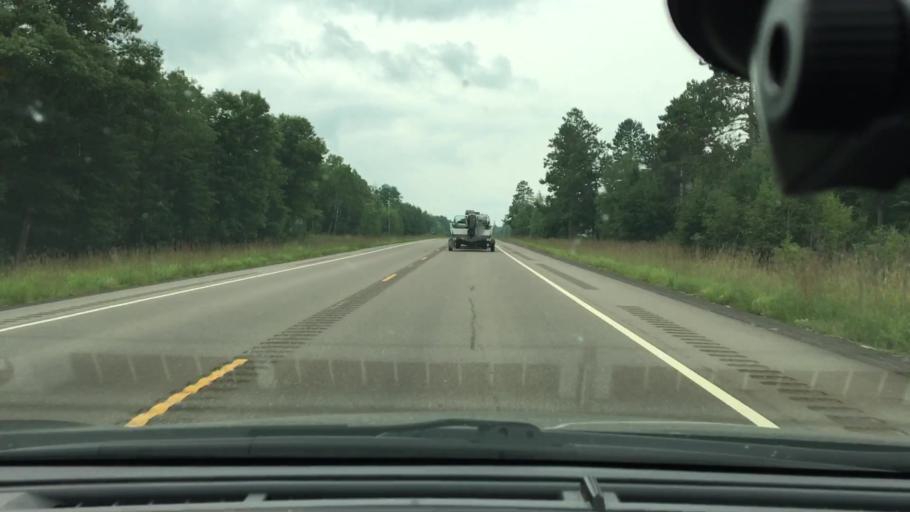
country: US
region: Minnesota
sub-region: Crow Wing County
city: Crosby
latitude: 46.5903
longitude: -93.9527
